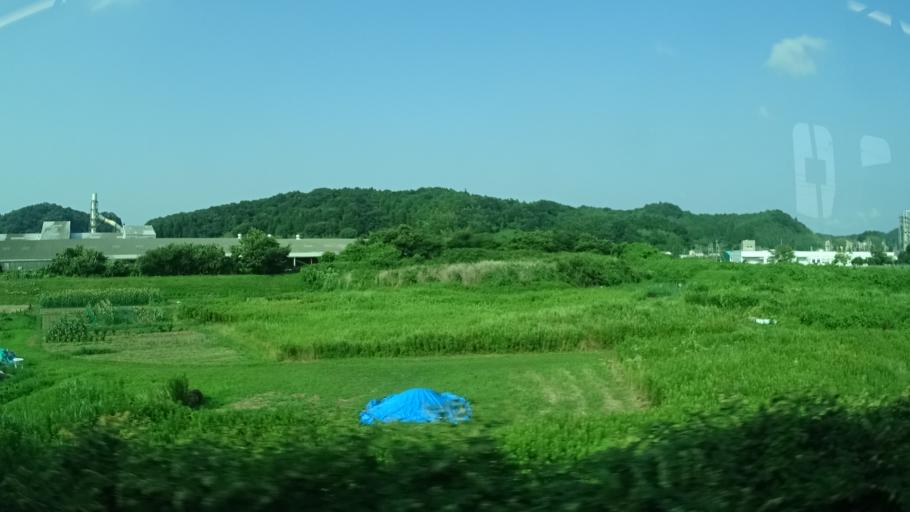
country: JP
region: Fukushima
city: Iwaki
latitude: 36.9911
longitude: 140.8598
